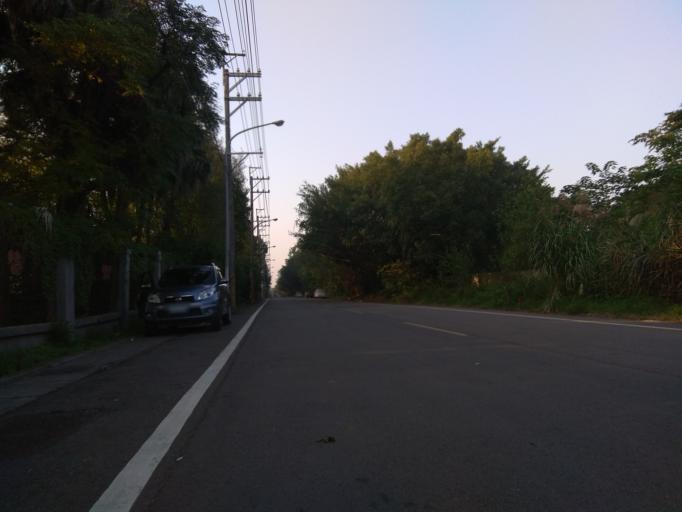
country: TW
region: Taiwan
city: Daxi
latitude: 24.9254
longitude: 121.1821
